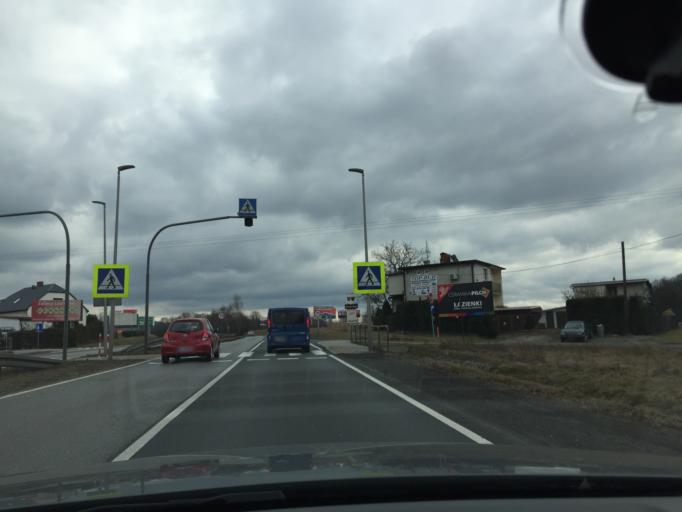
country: PL
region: Silesian Voivodeship
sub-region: Powiat bielski
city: Mazancowice
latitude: 49.8642
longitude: 19.0135
